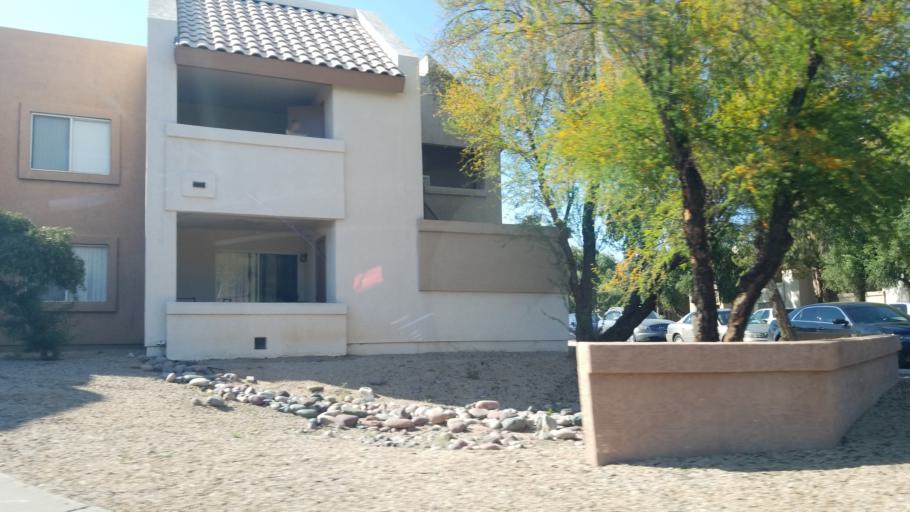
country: US
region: Arizona
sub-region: Maricopa County
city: Glendale
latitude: 33.5837
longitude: -112.1888
